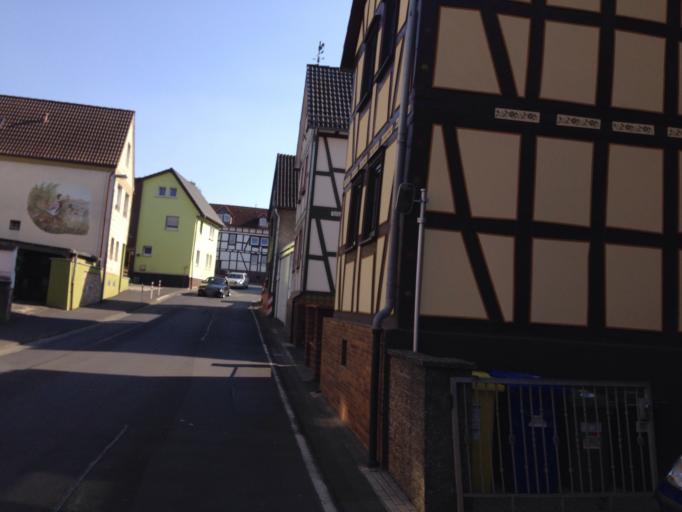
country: DE
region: Hesse
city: Staufenberg
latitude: 50.6520
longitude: 8.7378
